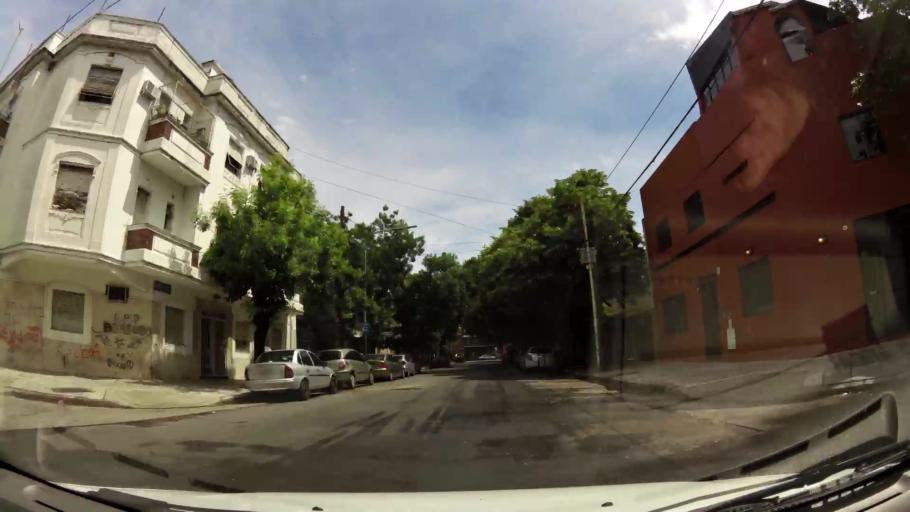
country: AR
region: Buenos Aires F.D.
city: Colegiales
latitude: -34.5912
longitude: -58.4451
